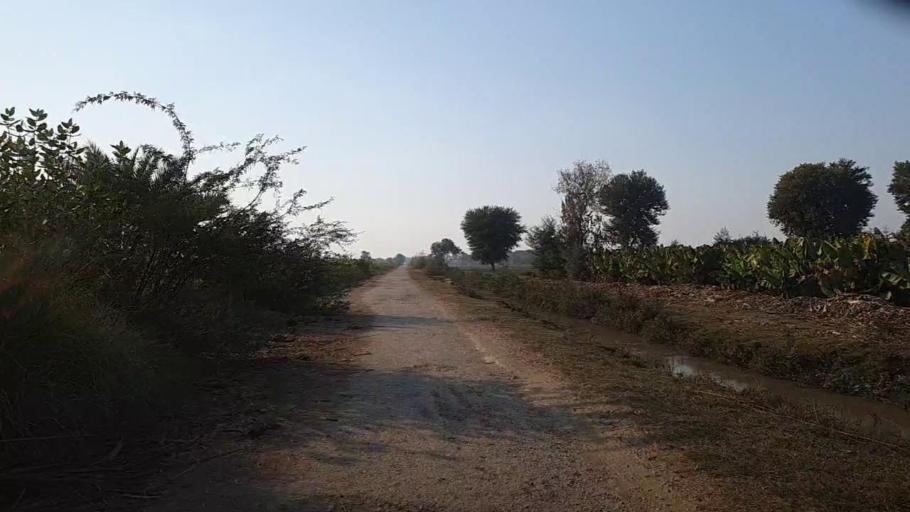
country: PK
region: Sindh
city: Ranipur
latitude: 27.2509
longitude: 68.5568
